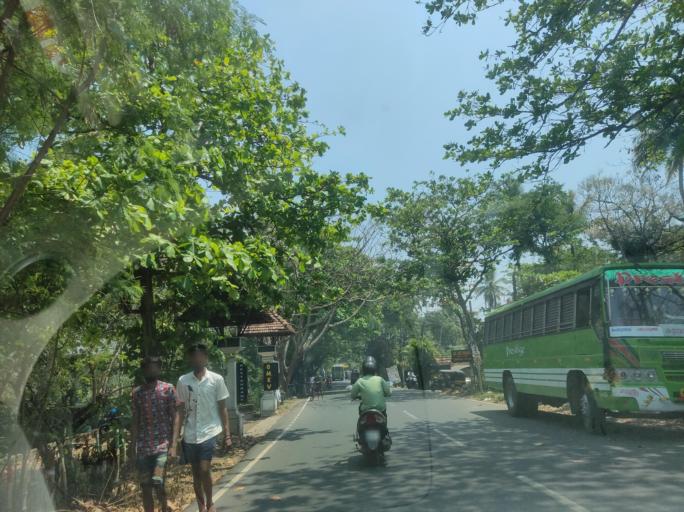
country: IN
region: Kerala
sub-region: Ernakulam
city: Cochin
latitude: 9.8991
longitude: 76.2832
